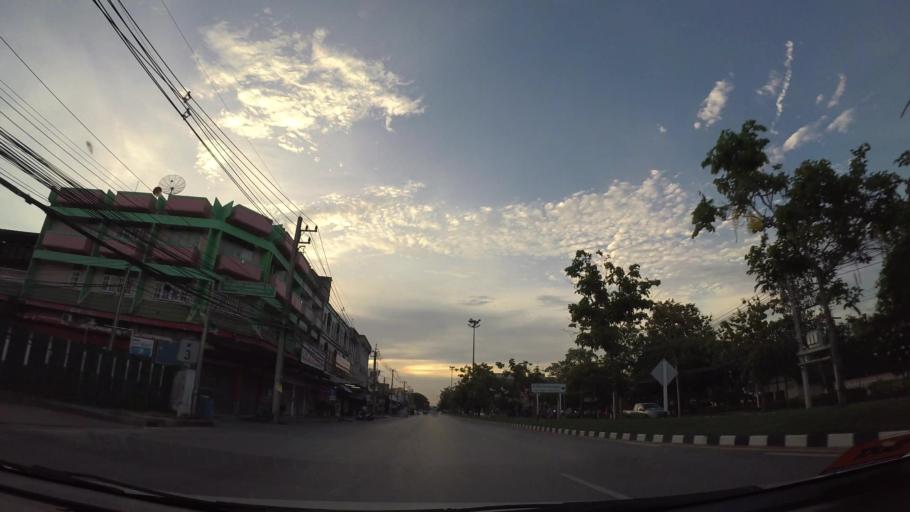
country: TH
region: Rayong
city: Rayong
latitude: 12.6757
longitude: 101.2888
